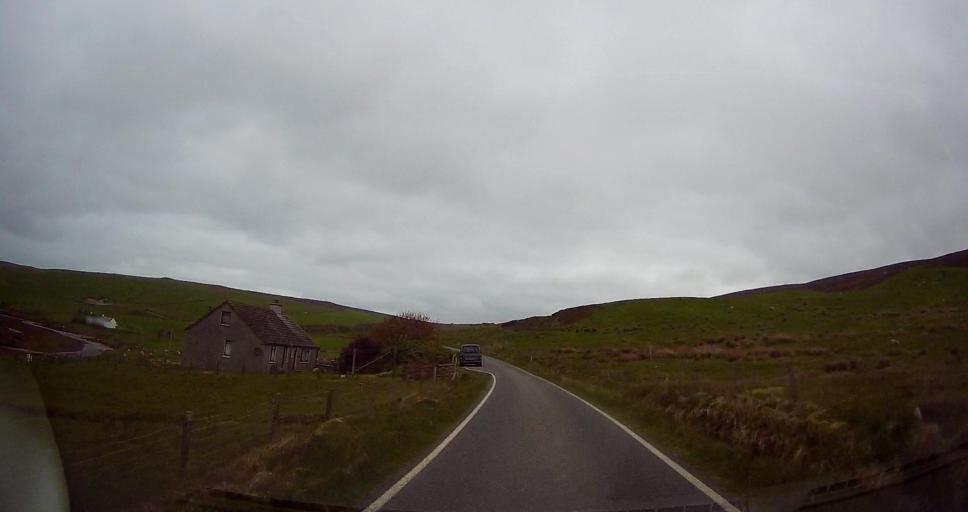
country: GB
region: Scotland
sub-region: Shetland Islands
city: Lerwick
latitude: 60.3014
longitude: -1.3369
